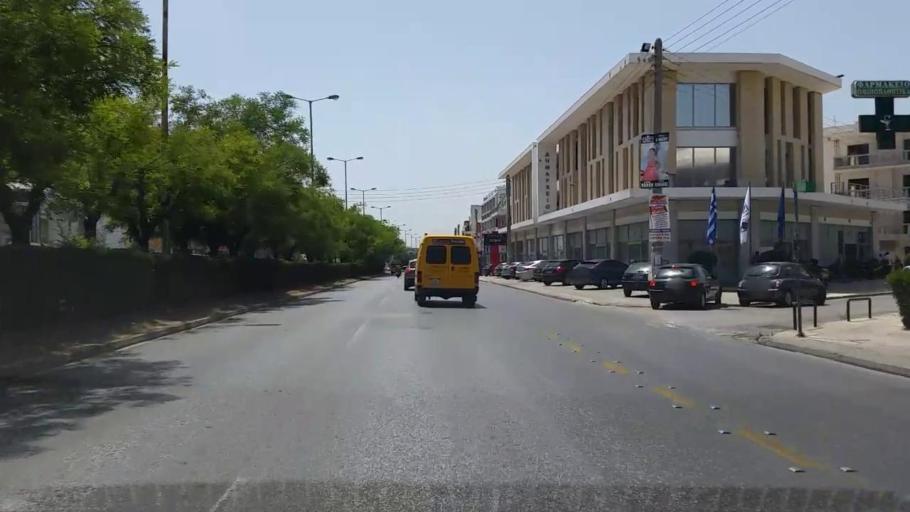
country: GR
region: Attica
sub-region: Nomarchia Athinas
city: Agia Paraskevi
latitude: 38.0129
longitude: 23.8176
